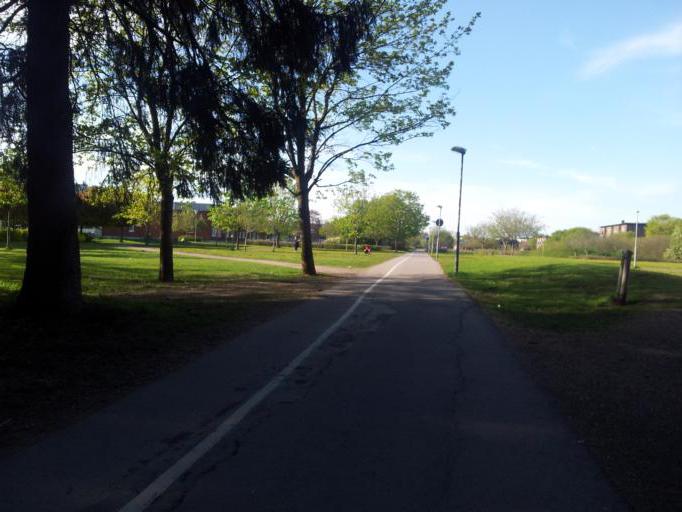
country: SE
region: Uppsala
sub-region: Uppsala Kommun
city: Uppsala
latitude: 59.8795
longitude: 17.6514
